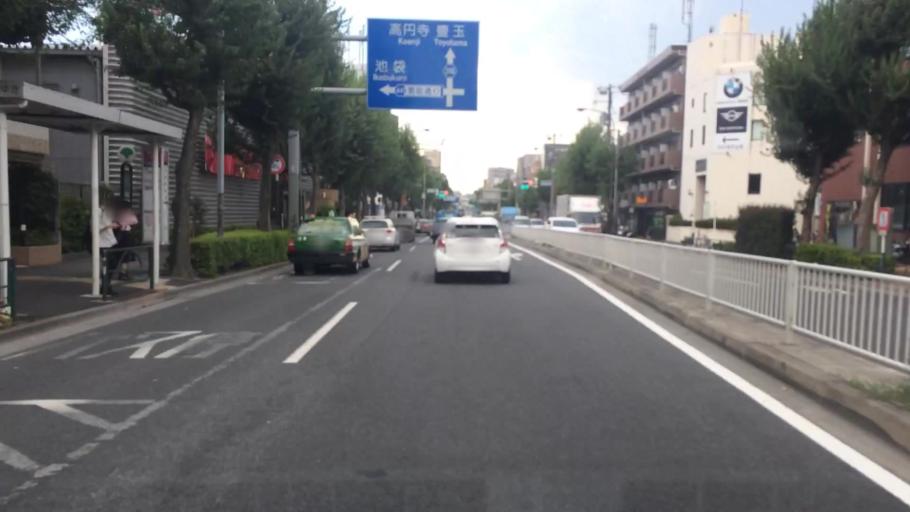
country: JP
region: Tokyo
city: Tokyo
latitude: 35.7462
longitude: 139.6758
